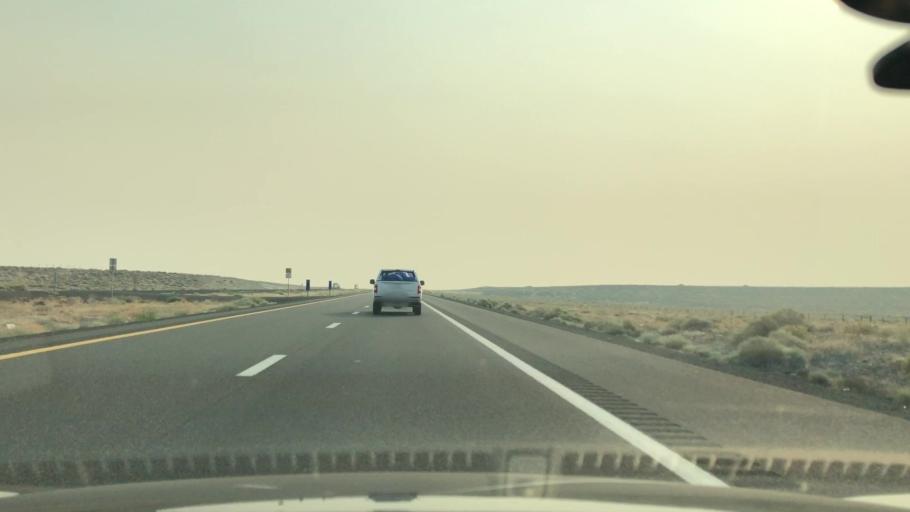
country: US
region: Nevada
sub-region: Churchill County
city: Fallon
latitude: 39.8564
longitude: -118.9165
